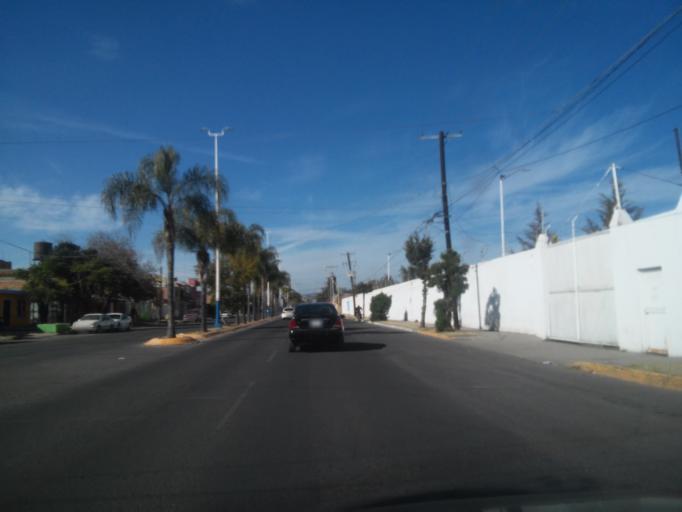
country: MX
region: Durango
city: Victoria de Durango
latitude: 24.0396
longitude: -104.6589
